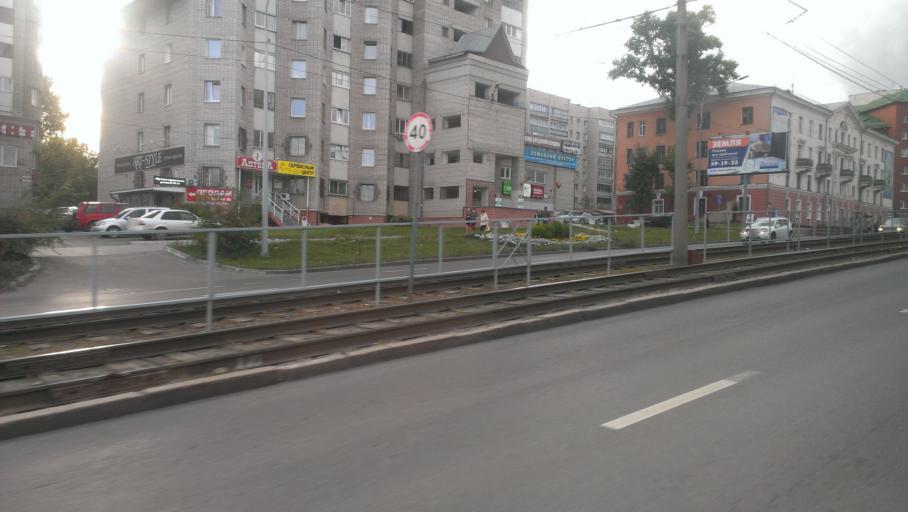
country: RU
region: Altai Krai
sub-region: Gorod Barnaulskiy
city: Barnaul
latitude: 53.3415
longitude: 83.7704
